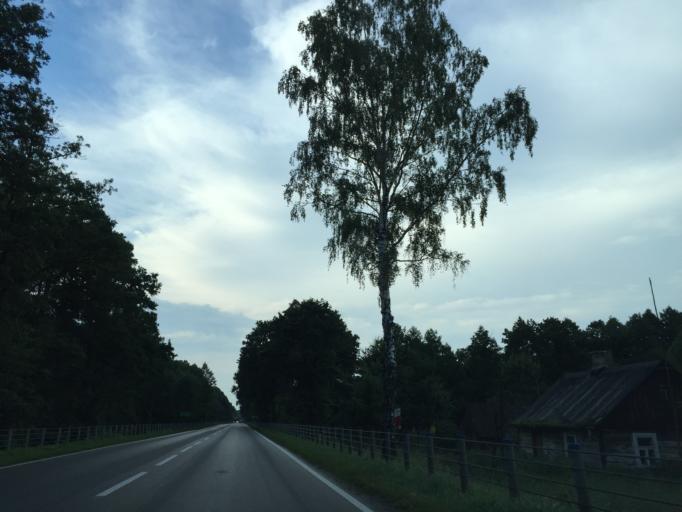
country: PL
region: Masovian Voivodeship
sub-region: Powiat ostrowski
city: Brok
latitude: 52.6784
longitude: 21.8508
